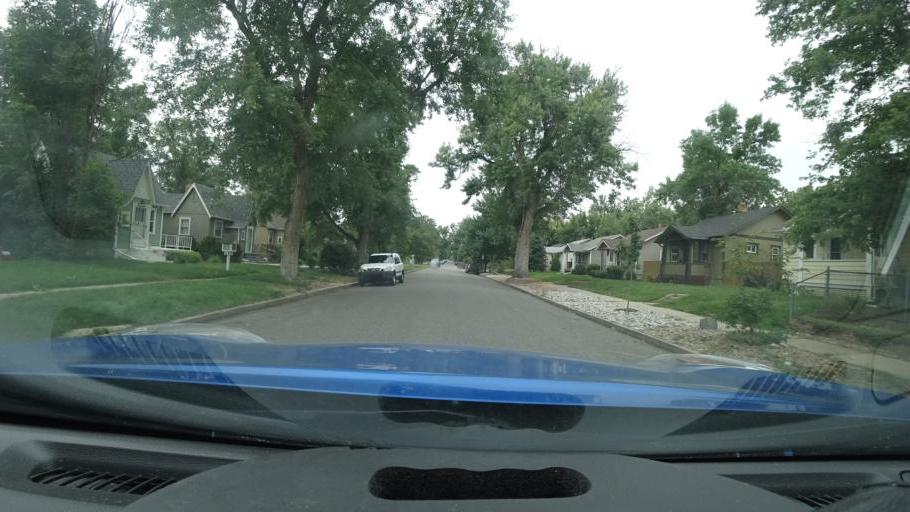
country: US
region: Colorado
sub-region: Arapahoe County
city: Glendale
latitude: 39.6835
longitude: -104.9663
